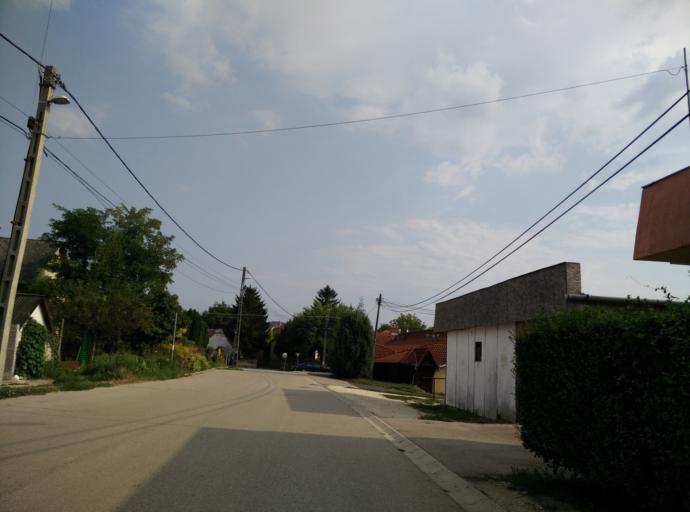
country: HU
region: Pest
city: Paty
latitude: 47.5160
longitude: 18.8299
